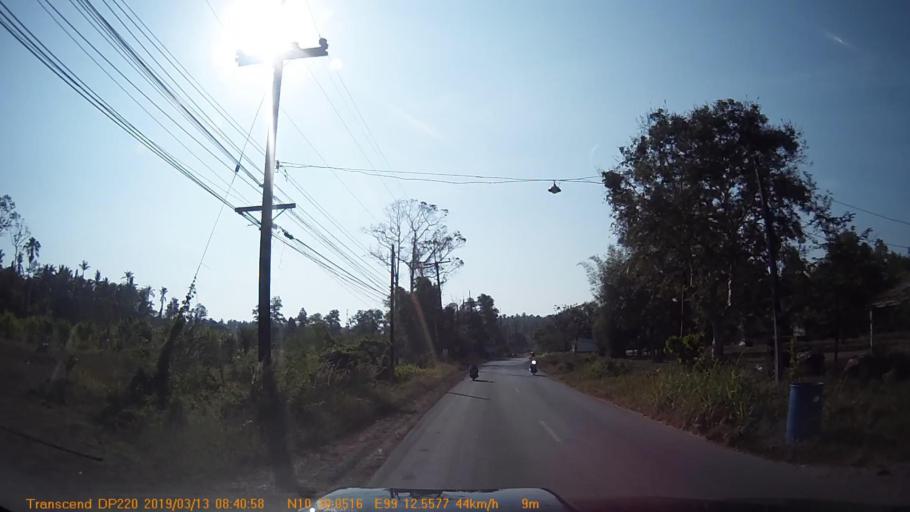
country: TH
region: Chumphon
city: Chumphon
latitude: 10.5007
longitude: 99.2095
